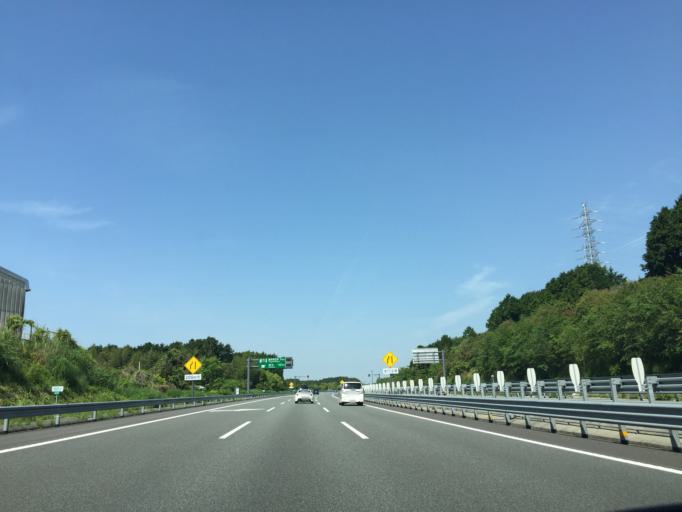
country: JP
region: Shizuoka
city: Numazu
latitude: 35.1522
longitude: 138.8500
